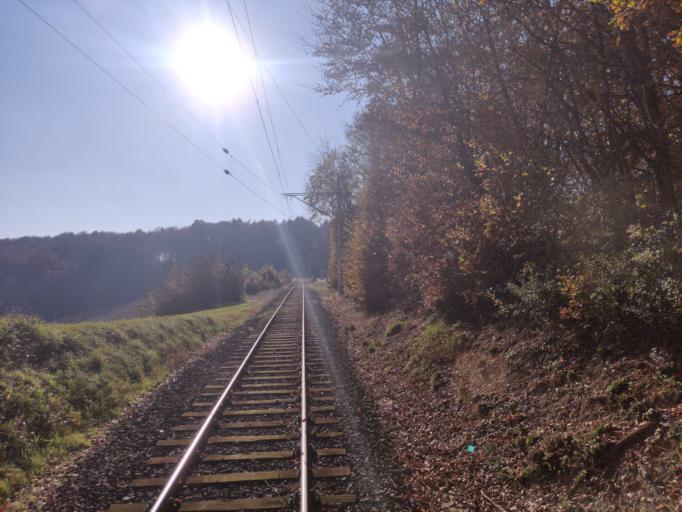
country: AT
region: Styria
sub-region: Politischer Bezirk Suedoststeiermark
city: Maierdorf
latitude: 46.9067
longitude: 15.8379
